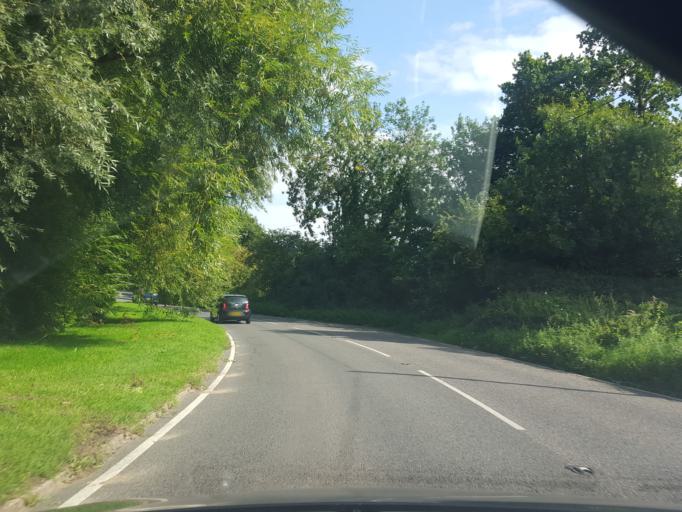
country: GB
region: England
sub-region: Suffolk
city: Shotley Gate
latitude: 51.9317
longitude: 1.2129
